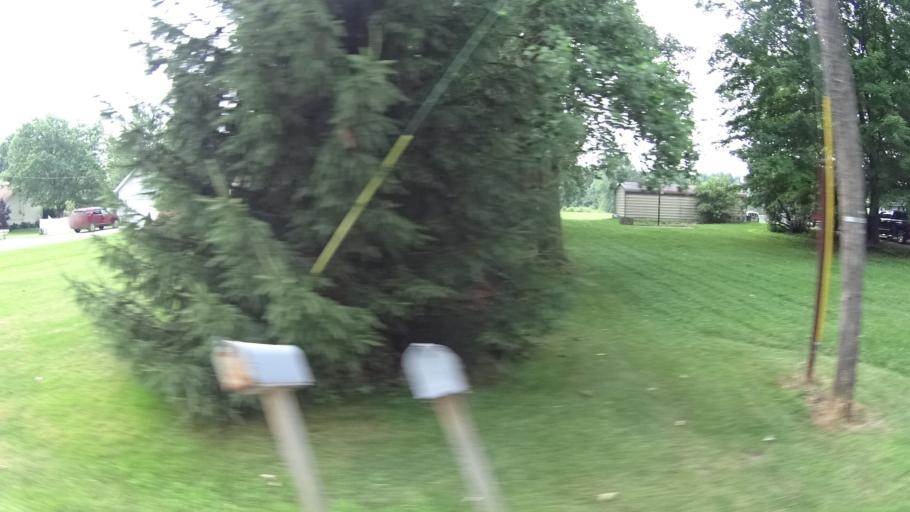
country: US
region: Ohio
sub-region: Lorain County
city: Vermilion
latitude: 41.3694
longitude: -82.3515
